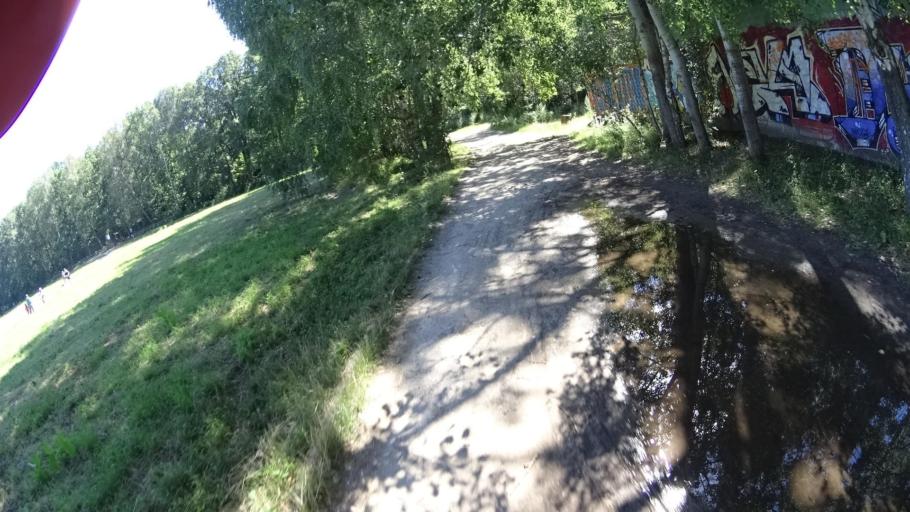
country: PL
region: Masovian Voivodeship
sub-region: Warszawa
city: Kabaty
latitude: 52.1249
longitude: 21.0733
